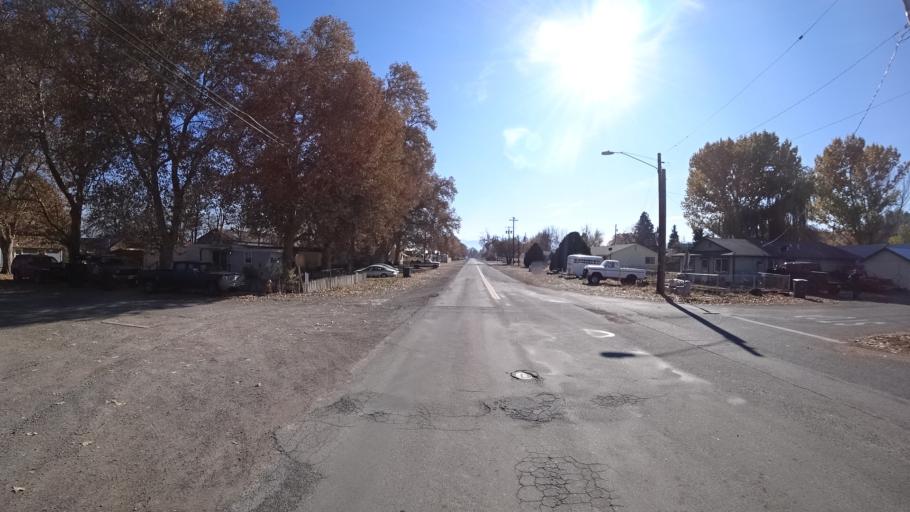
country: US
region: California
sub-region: Siskiyou County
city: Montague
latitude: 41.6455
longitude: -122.5224
